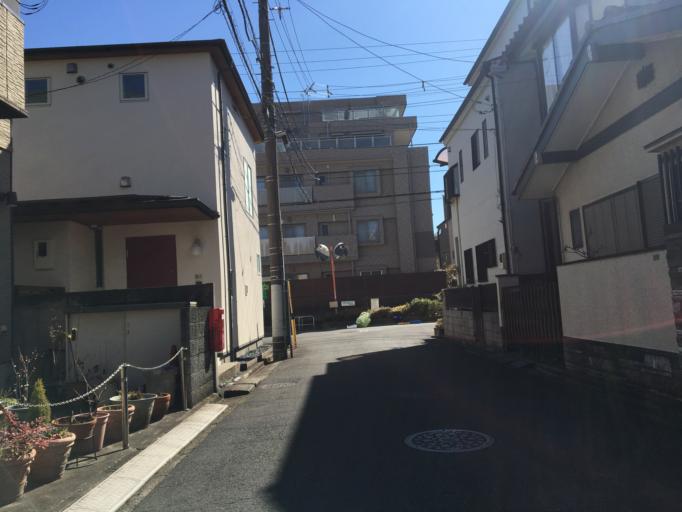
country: JP
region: Saitama
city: Shiki
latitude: 35.8105
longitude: 139.5680
